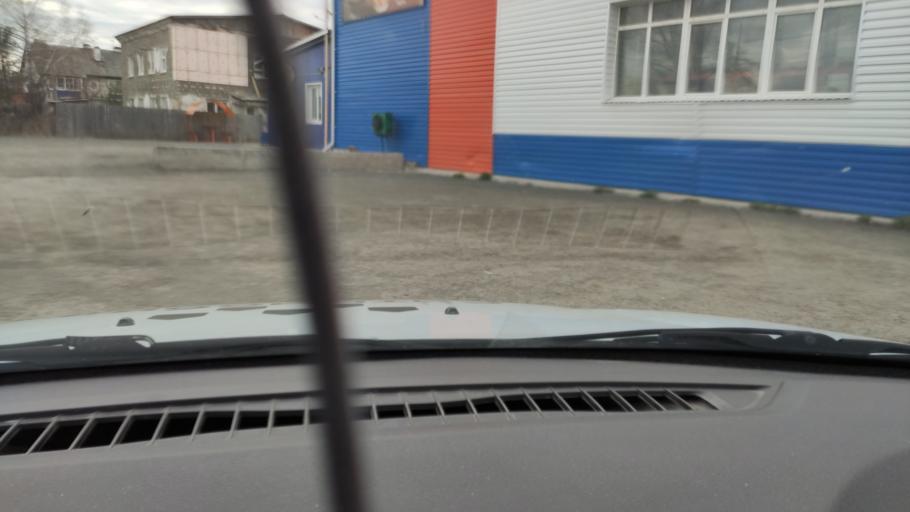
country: RU
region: Perm
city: Kungur
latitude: 57.4252
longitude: 56.9297
